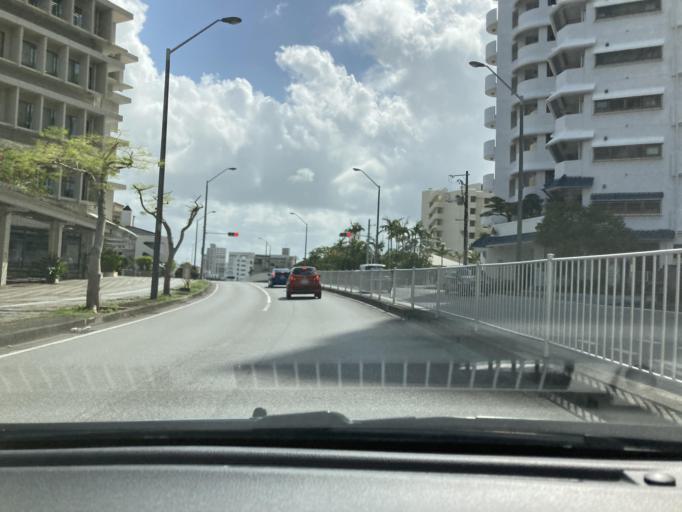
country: JP
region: Okinawa
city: Naha-shi
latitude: 26.2249
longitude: 127.6928
